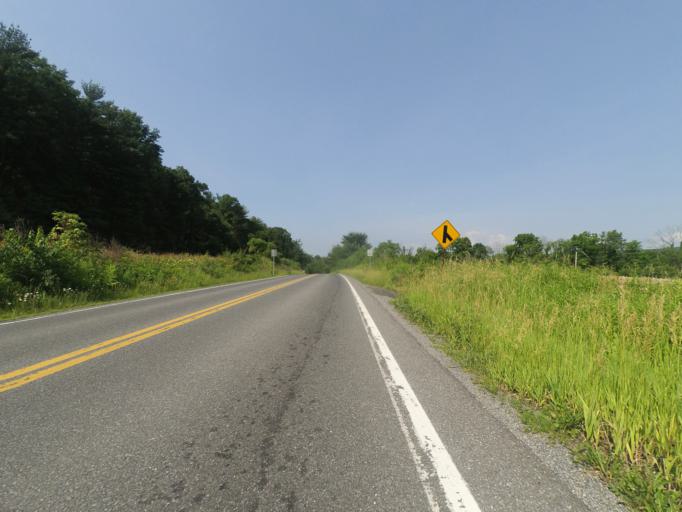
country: US
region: Pennsylvania
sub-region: Centre County
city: Milesburg
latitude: 40.9673
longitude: -77.7393
